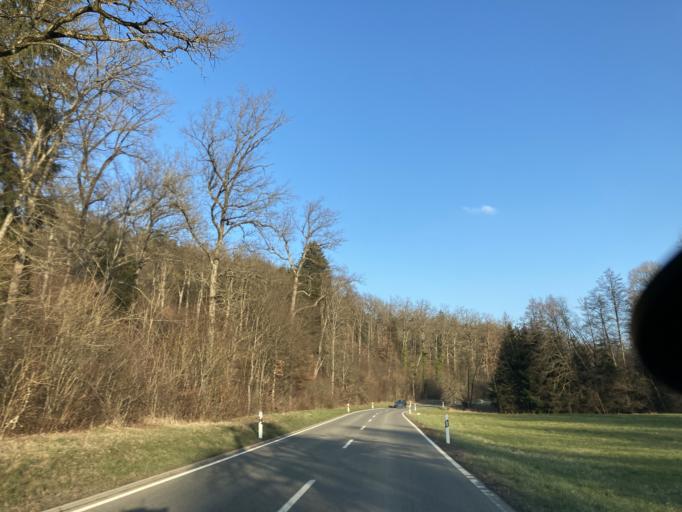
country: DE
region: Baden-Wuerttemberg
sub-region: Tuebingen Region
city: Bodelshausen
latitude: 48.4301
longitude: 8.9633
